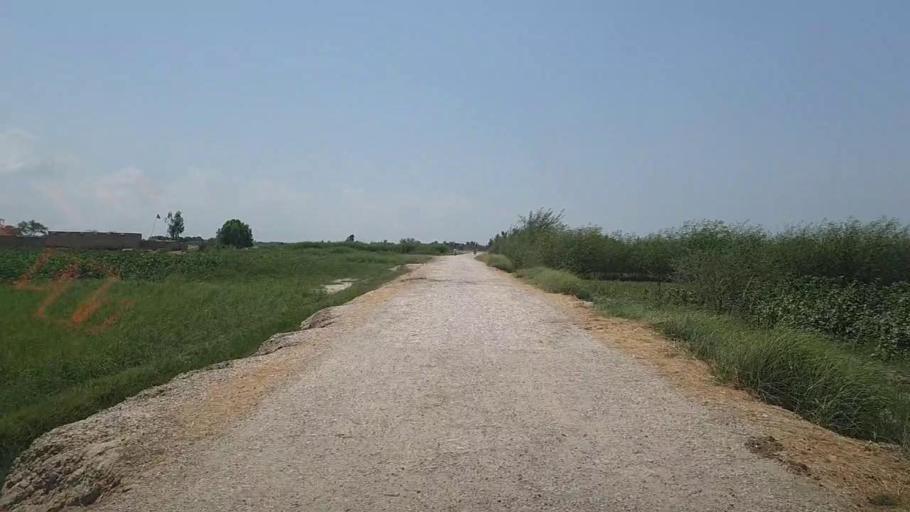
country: PK
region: Sindh
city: Ubauro
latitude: 28.1669
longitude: 69.7636
